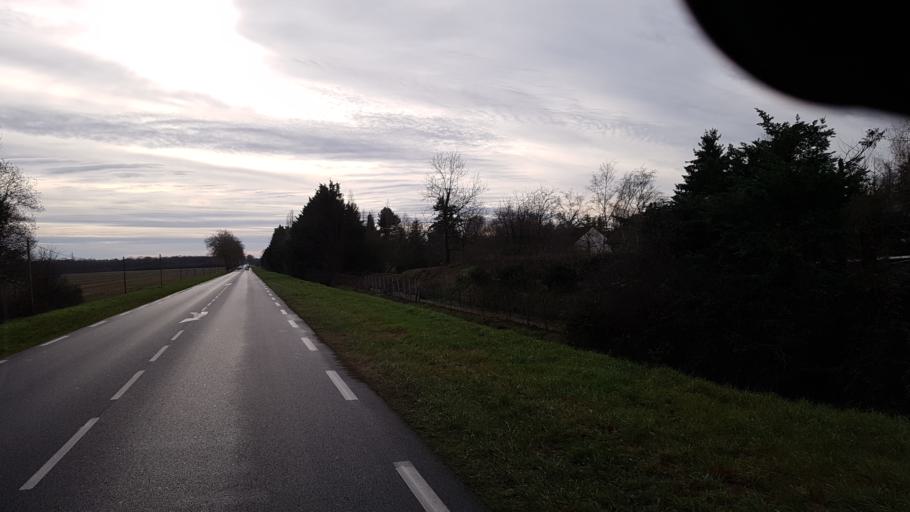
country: FR
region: Centre
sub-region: Departement du Loiret
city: Saint-Cyr-en-Val
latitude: 47.8069
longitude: 1.9298
